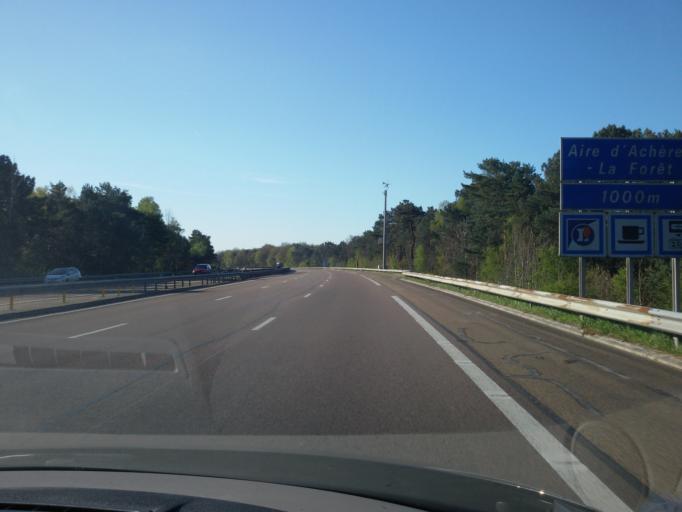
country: FR
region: Ile-de-France
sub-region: Departement de Seine-et-Marne
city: Acheres-la-Foret
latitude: 48.3730
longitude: 2.5619
